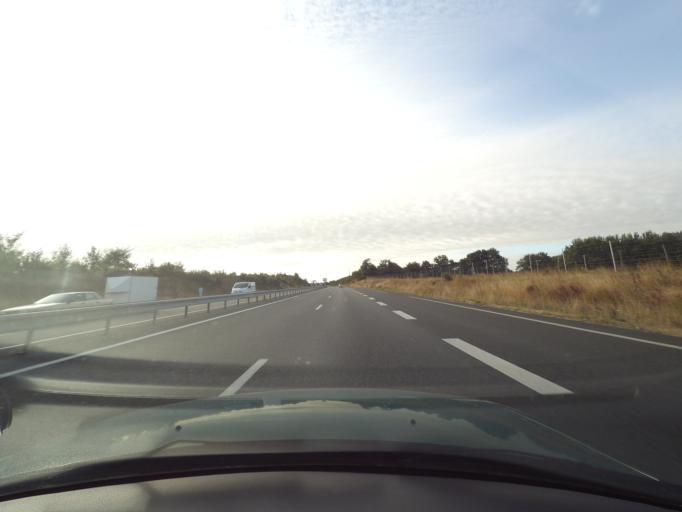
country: FR
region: Pays de la Loire
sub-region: Departement de Maine-et-Loire
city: La Tessoualle
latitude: 46.9882
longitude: -0.8429
